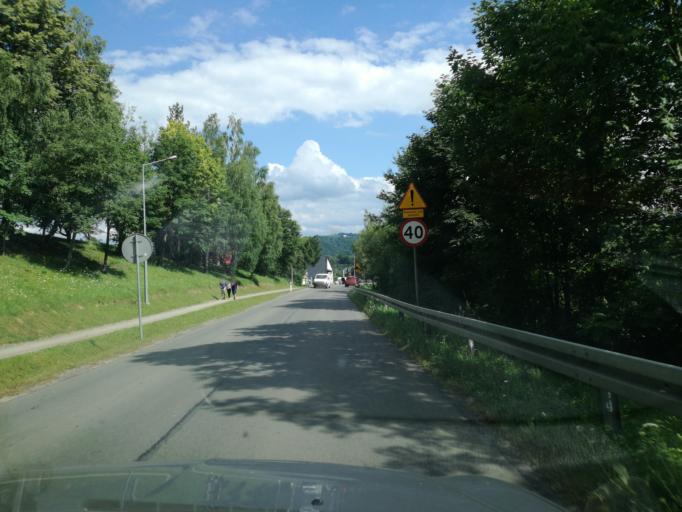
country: PL
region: Subcarpathian Voivodeship
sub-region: Powiat leski
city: Polanczyk
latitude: 49.3653
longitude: 22.4241
